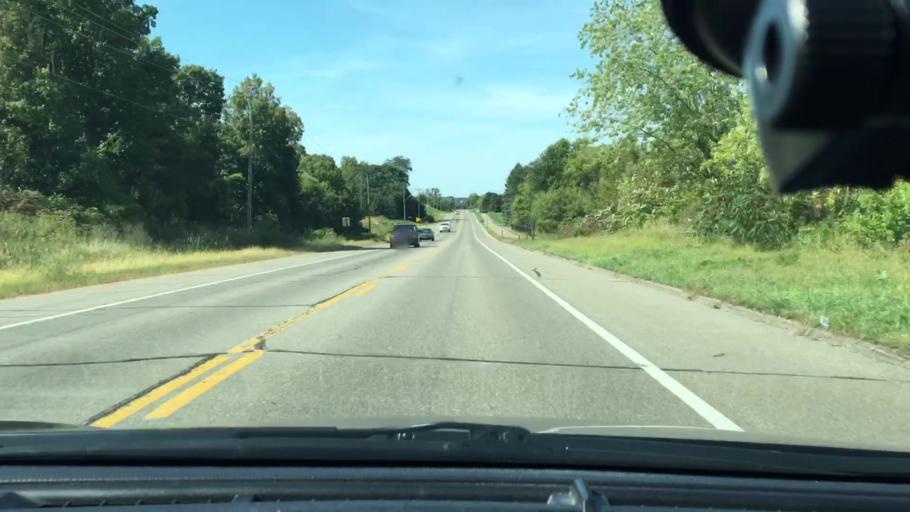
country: US
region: Minnesota
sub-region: Wright County
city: Hanover
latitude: 45.1526
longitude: -93.6431
